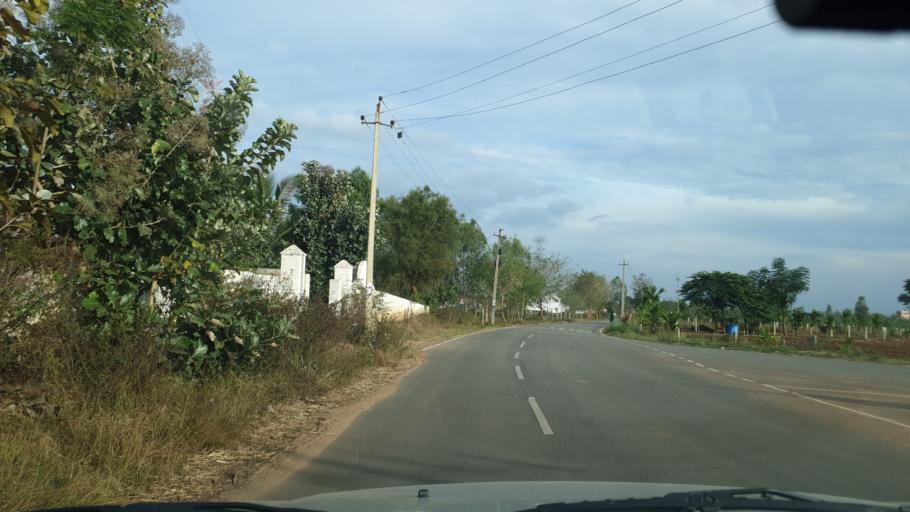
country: IN
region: Karnataka
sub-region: Bangalore Urban
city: Yelahanka
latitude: 13.1961
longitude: 77.6193
